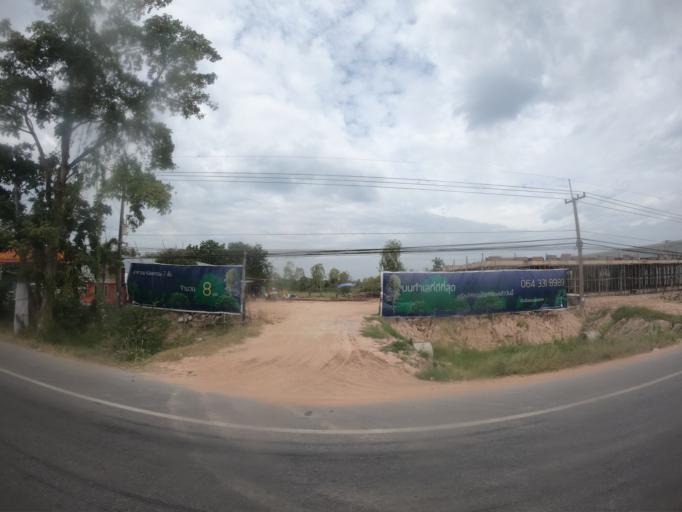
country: TH
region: Maha Sarakham
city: Maha Sarakham
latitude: 16.1635
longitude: 103.3415
